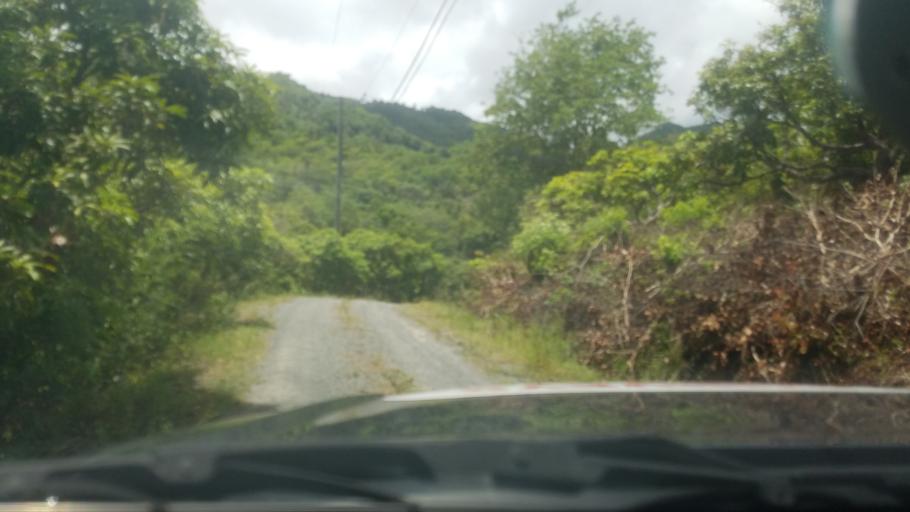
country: LC
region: Praslin
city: Praslin
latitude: 13.8664
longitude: -60.9076
